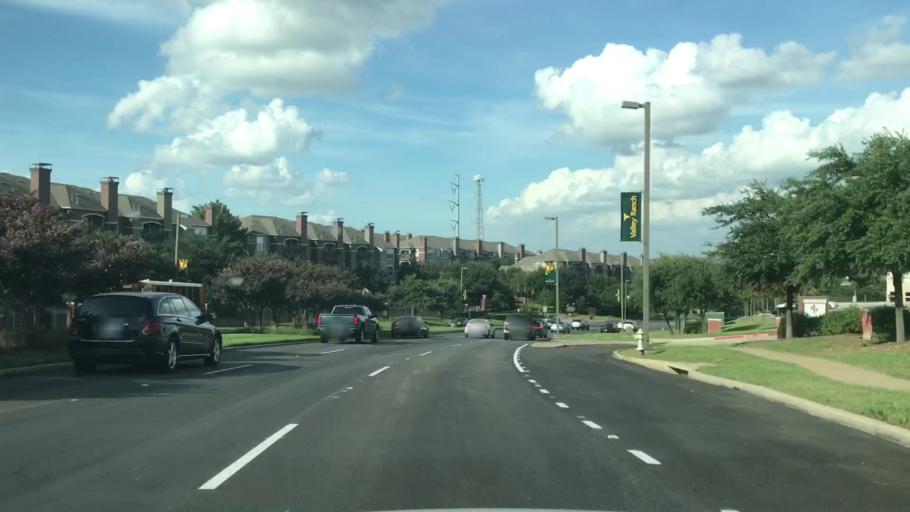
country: US
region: Texas
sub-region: Dallas County
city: Farmers Branch
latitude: 32.9204
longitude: -96.9584
